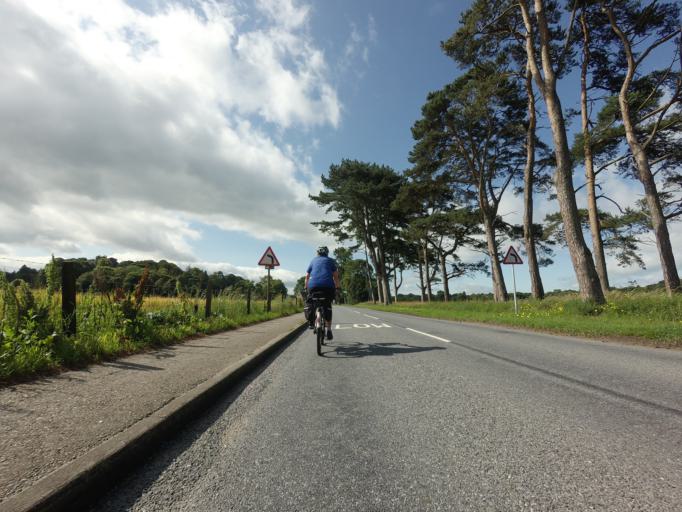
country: GB
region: Scotland
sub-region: Highland
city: Nairn
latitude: 57.5772
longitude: -3.8609
